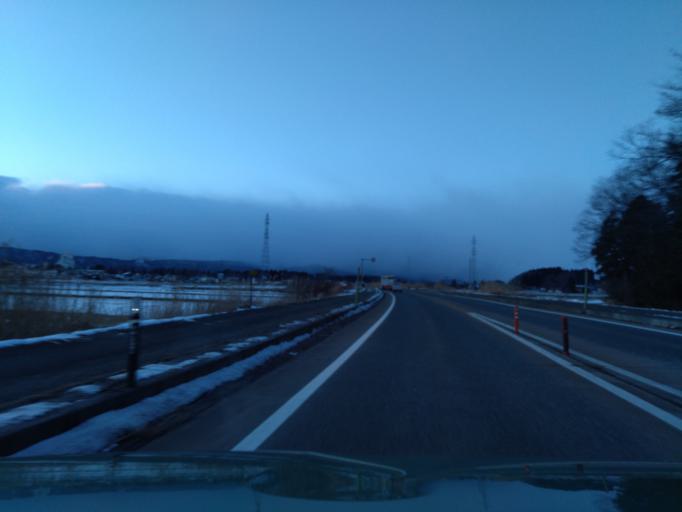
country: JP
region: Iwate
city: Shizukuishi
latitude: 39.7000
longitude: 140.9760
